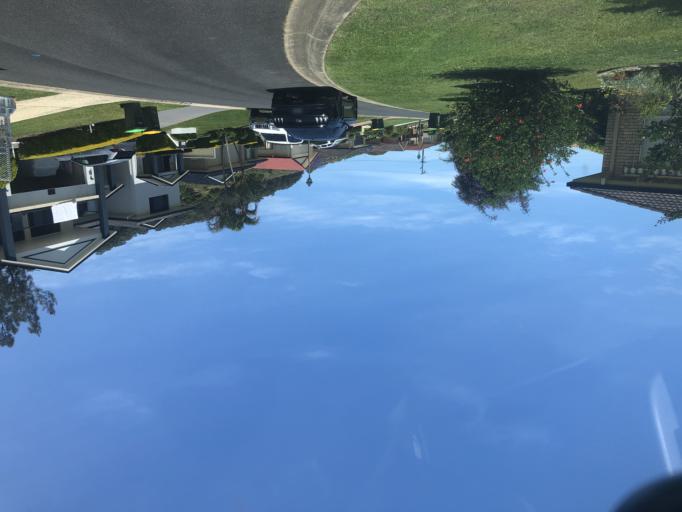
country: AU
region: New South Wales
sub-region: Coffs Harbour
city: Coffs Harbour
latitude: -30.2902
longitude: 153.0905
